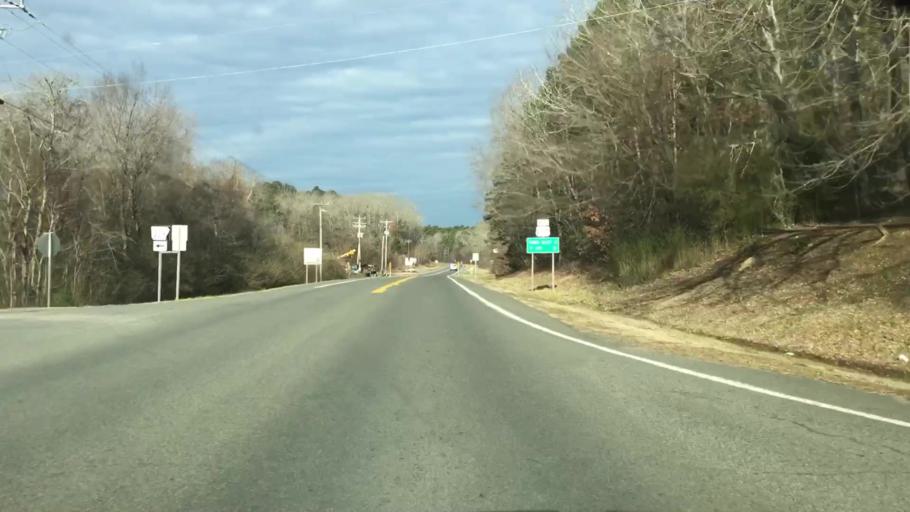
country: US
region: Arkansas
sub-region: Montgomery County
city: Mount Ida
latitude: 34.5625
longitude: -93.6402
